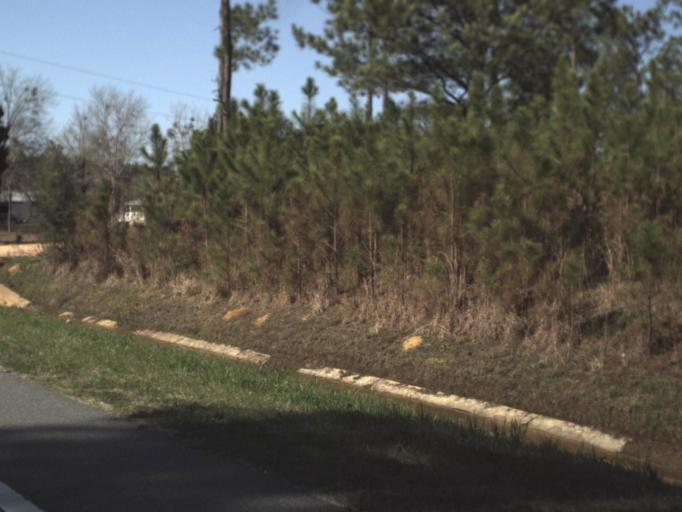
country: US
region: Florida
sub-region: Gulf County
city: Wewahitchka
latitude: 30.2471
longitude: -85.2252
